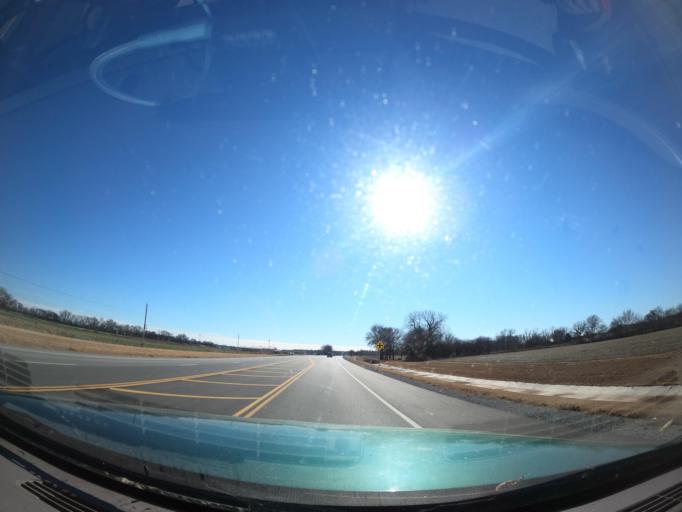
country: US
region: Oklahoma
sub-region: Wagoner County
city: Coweta
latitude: 35.8876
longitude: -95.6593
